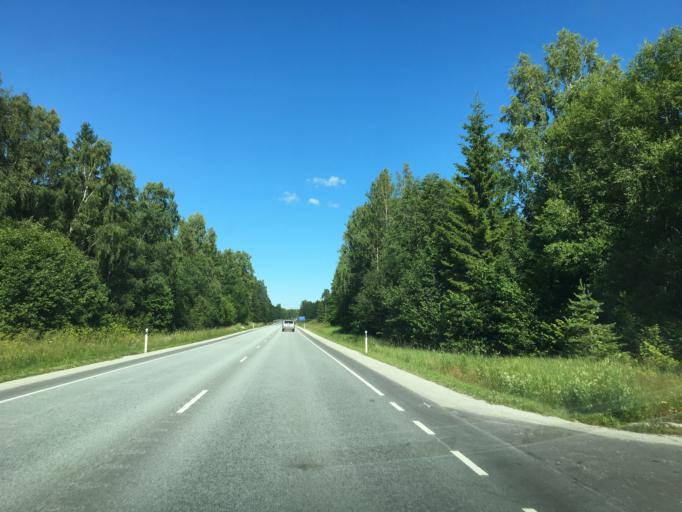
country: EE
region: Harju
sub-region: Keila linn
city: Keila
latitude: 59.2340
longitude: 24.4679
